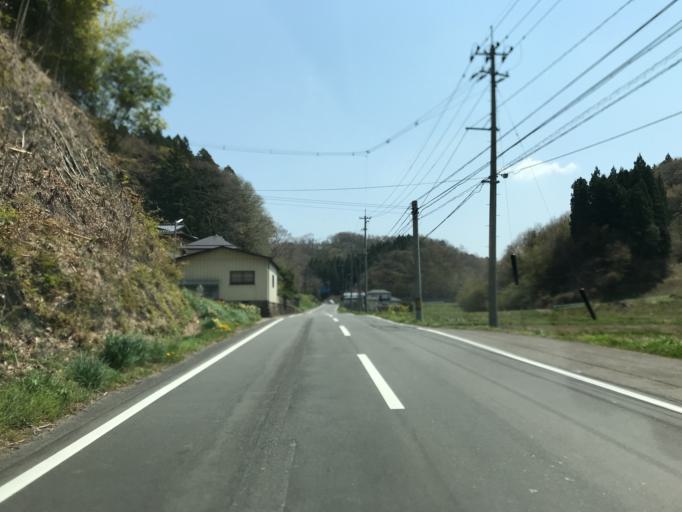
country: JP
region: Fukushima
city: Ishikawa
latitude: 37.0629
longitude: 140.4526
